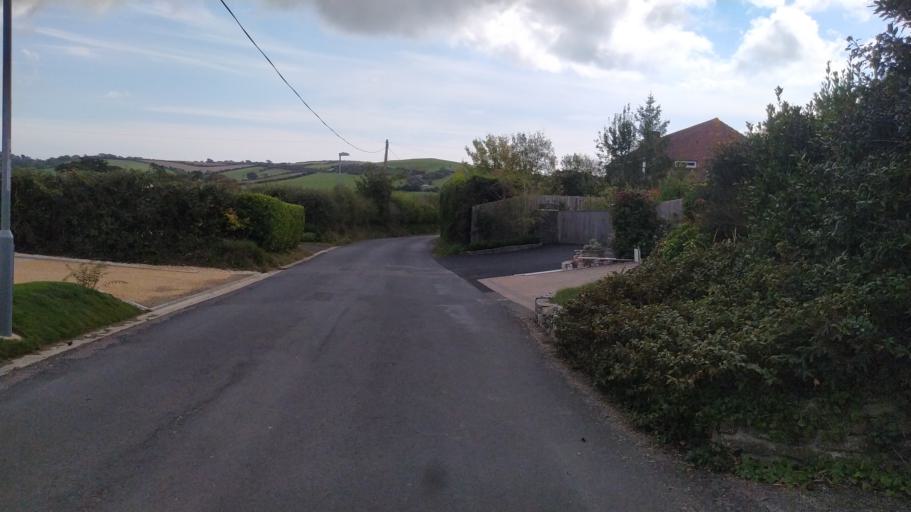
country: GB
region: England
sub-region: Dorset
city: Overcombe
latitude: 50.6552
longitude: -2.4208
